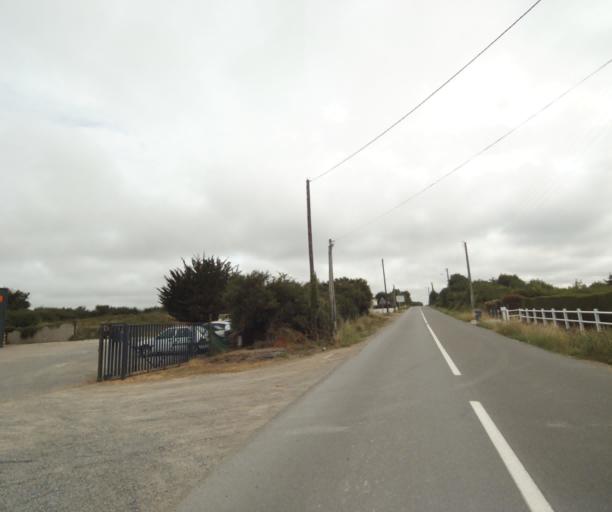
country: FR
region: Pays de la Loire
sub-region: Departement de la Vendee
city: Chateau-d'Olonne
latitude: 46.4821
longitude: -1.7157
